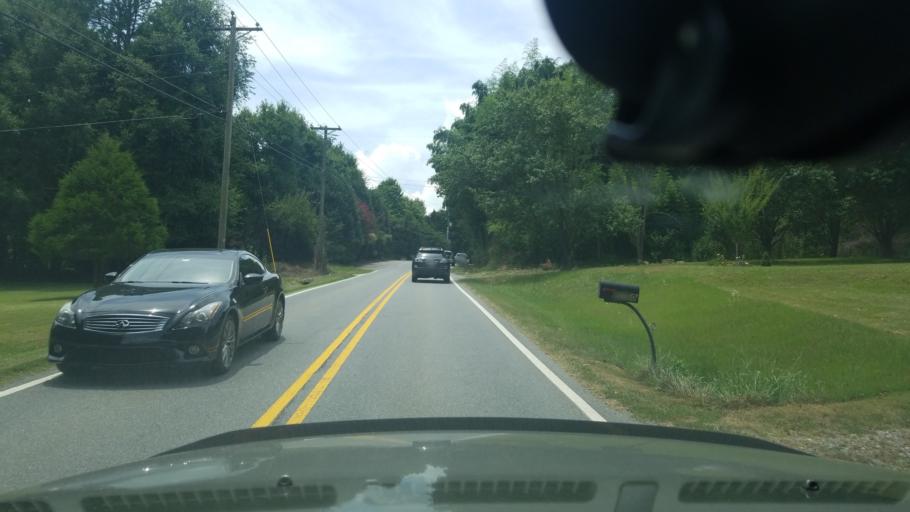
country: US
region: Georgia
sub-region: Forsyth County
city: Cumming
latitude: 34.1930
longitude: -84.2311
